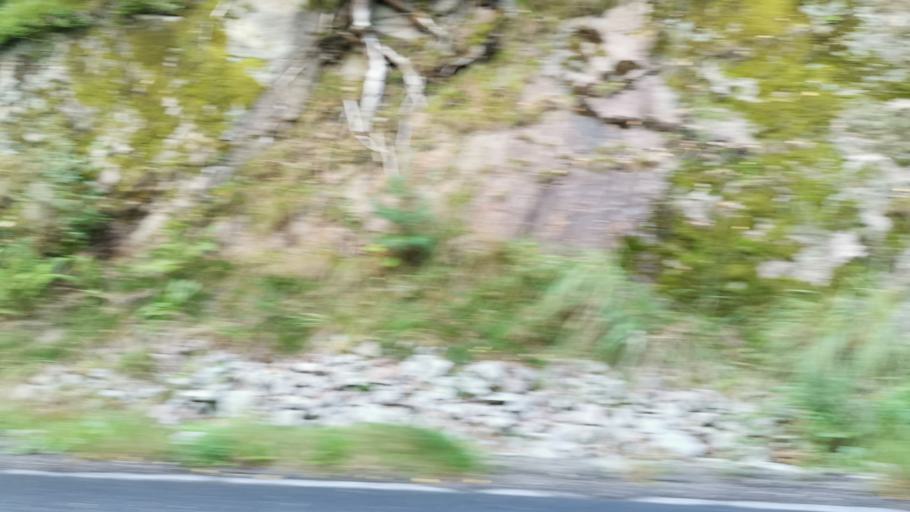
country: SE
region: Vaestra Goetaland
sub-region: Sotenas Kommun
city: Hunnebostrand
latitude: 58.4868
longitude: 11.3730
